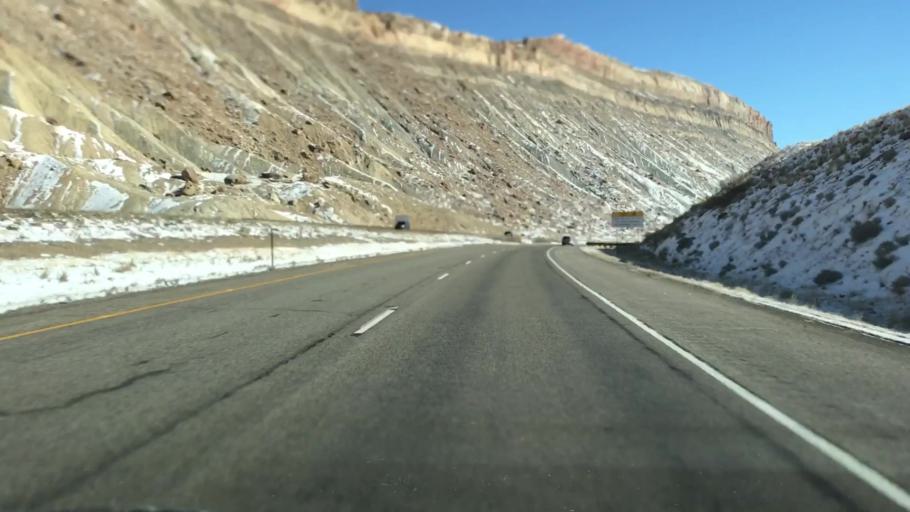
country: US
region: Colorado
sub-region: Mesa County
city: Palisade
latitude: 39.1202
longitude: -108.3767
